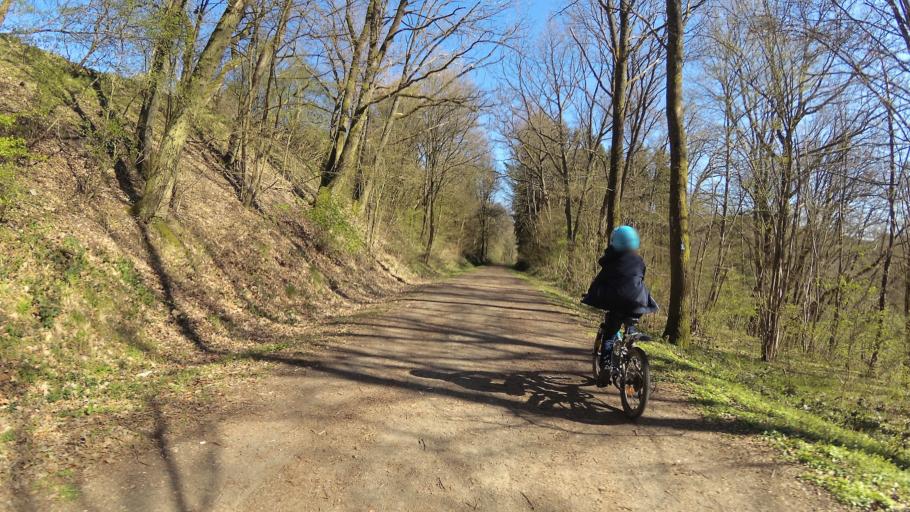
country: DE
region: Rheinland-Pfalz
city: Ruthweiler
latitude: 49.5493
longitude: 7.3781
